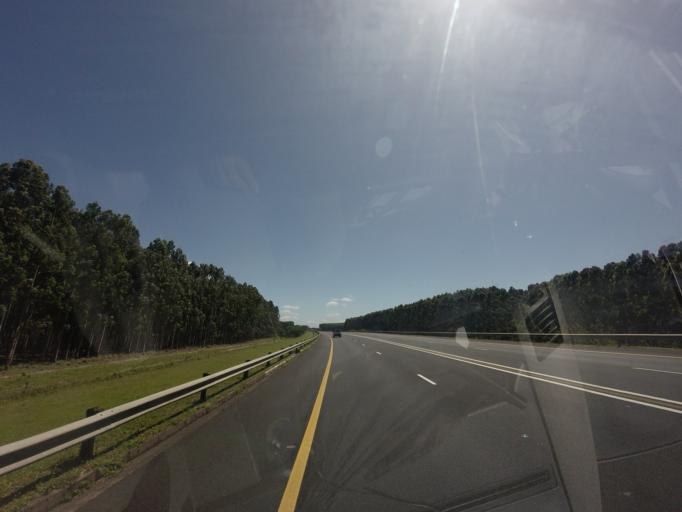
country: ZA
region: KwaZulu-Natal
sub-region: uThungulu District Municipality
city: Eshowe
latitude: -29.0167
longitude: 31.6755
